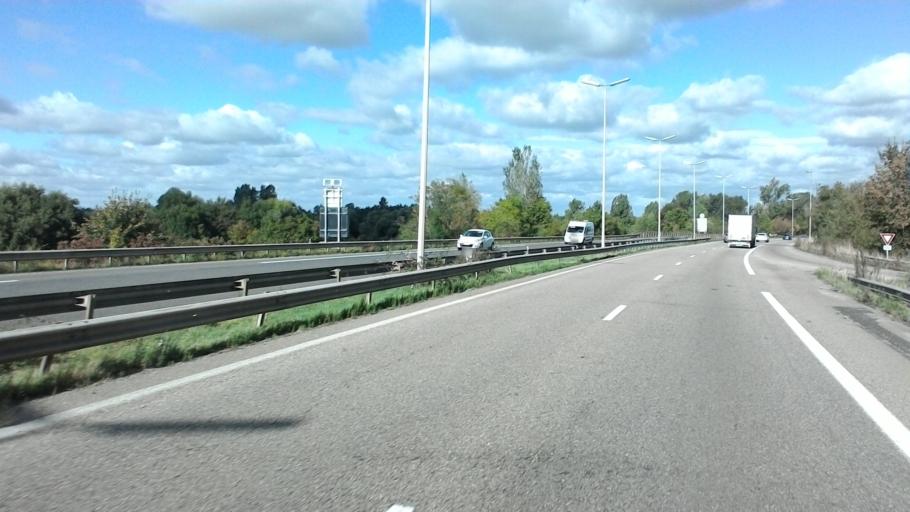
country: FR
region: Lorraine
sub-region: Departement de Meurthe-et-Moselle
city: Dommartin-les-Toul
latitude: 48.6749
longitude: 5.9211
